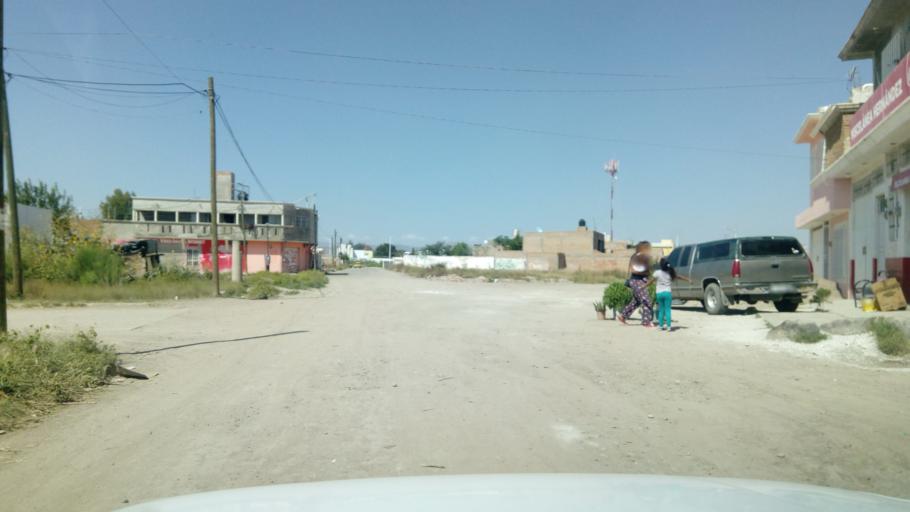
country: MX
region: Durango
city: Victoria de Durango
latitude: 23.9875
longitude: -104.6699
